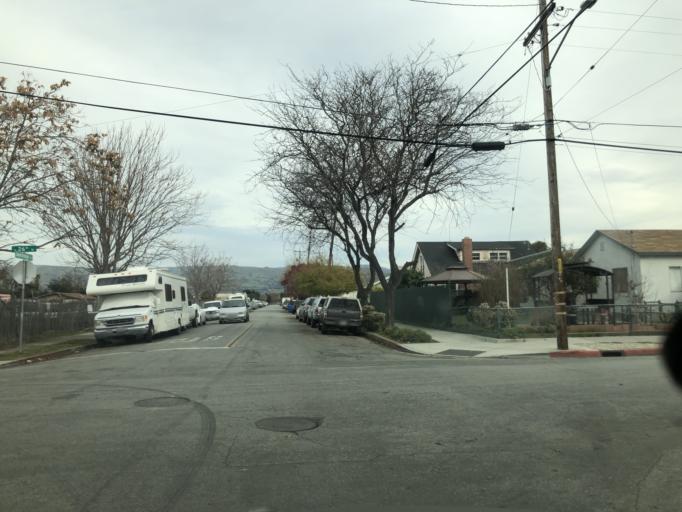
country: US
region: California
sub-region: Santa Clara County
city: San Jose
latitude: 37.3470
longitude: -121.8653
